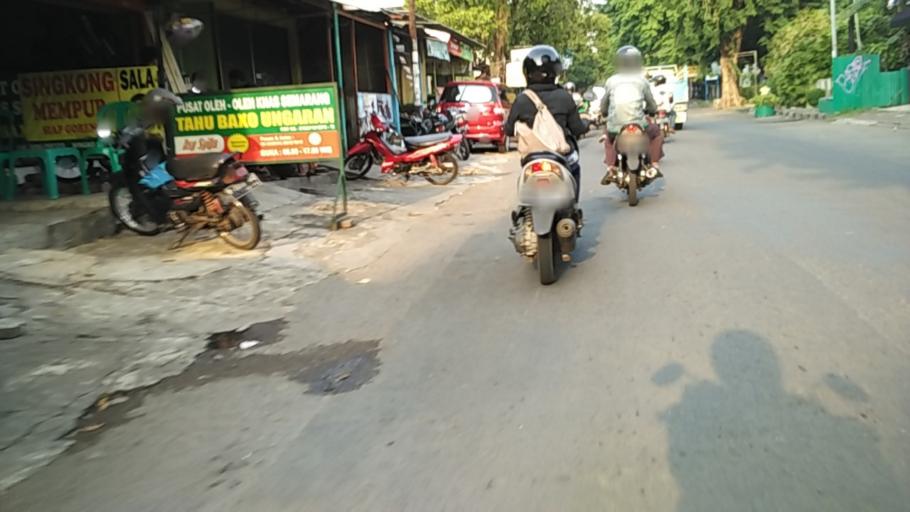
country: ID
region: Central Java
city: Semarang
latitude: -6.9938
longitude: 110.4117
